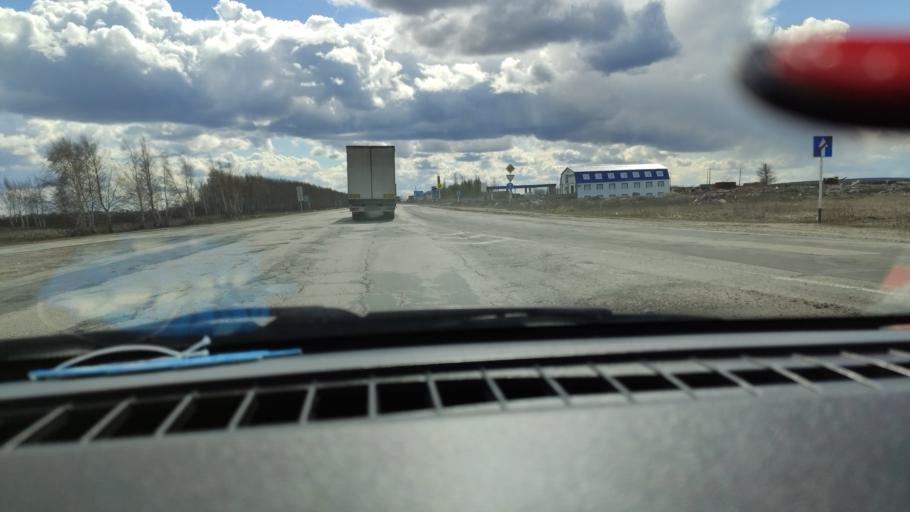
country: RU
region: Samara
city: Syzran'
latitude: 52.9952
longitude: 48.3252
